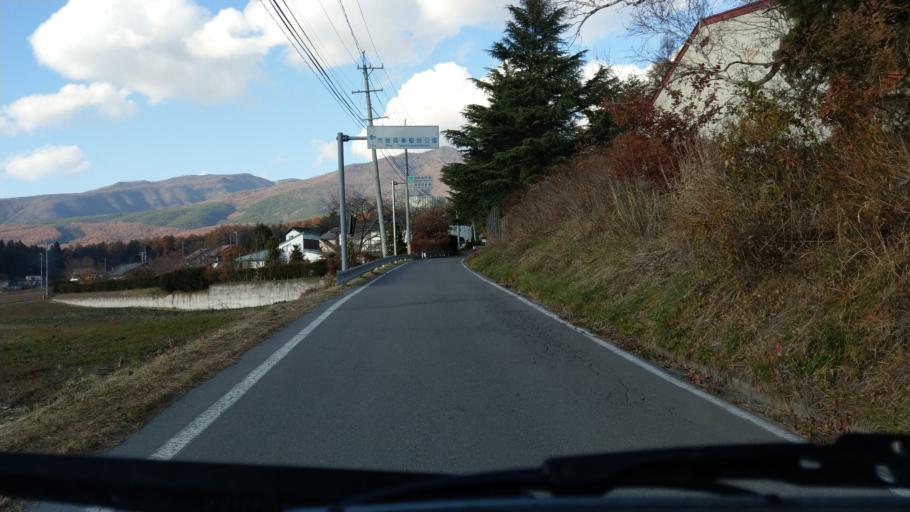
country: JP
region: Nagano
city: Komoro
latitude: 36.3514
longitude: 138.4582
